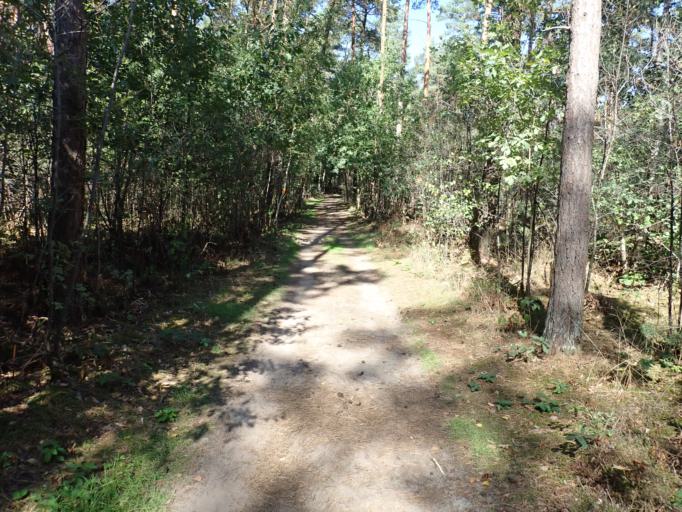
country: BE
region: Flanders
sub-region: Provincie Antwerpen
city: Lille
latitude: 51.2212
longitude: 4.8879
